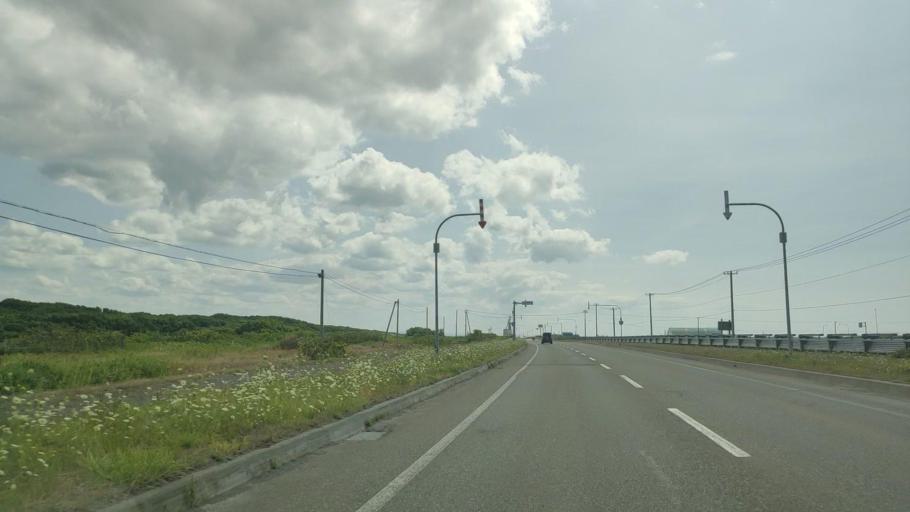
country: JP
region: Hokkaido
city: Makubetsu
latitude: 44.8696
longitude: 141.7526
